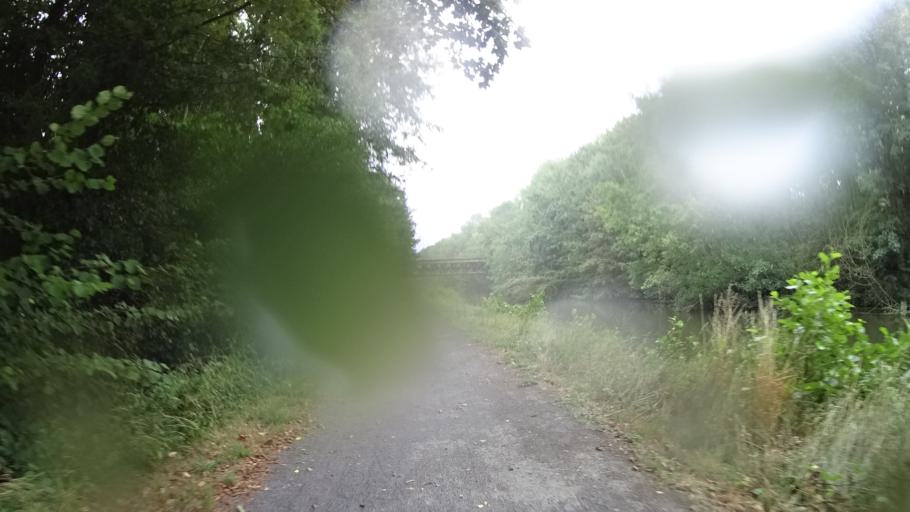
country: FR
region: Nord-Pas-de-Calais
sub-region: Departement du Nord
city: Louvroil
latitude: 50.2632
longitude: 3.9468
